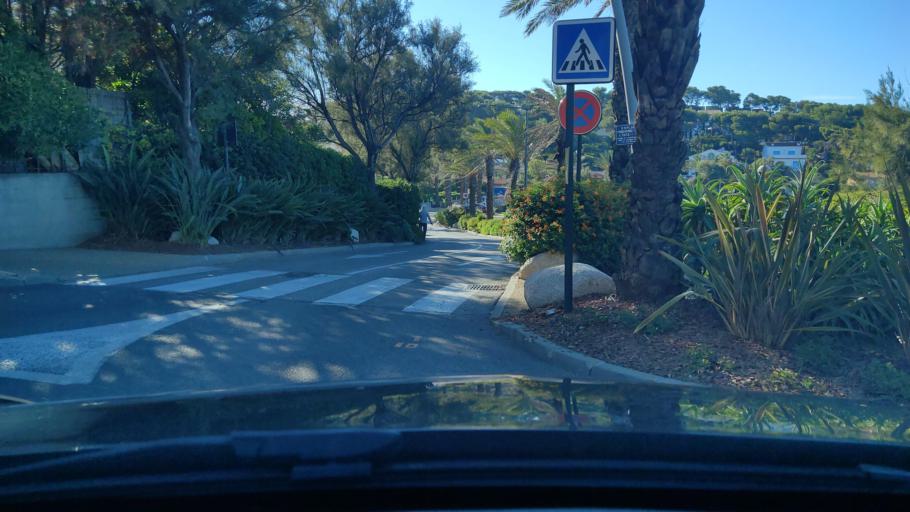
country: FR
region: Provence-Alpes-Cote d'Azur
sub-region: Departement du Var
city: Sanary-sur-Mer
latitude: 43.1162
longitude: 5.7901
